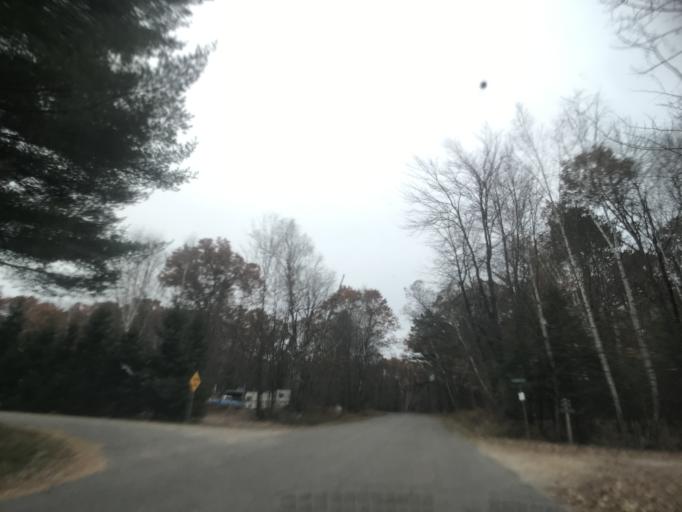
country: US
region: Michigan
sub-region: Dickinson County
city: Kingsford
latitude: 45.3802
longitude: -88.3217
